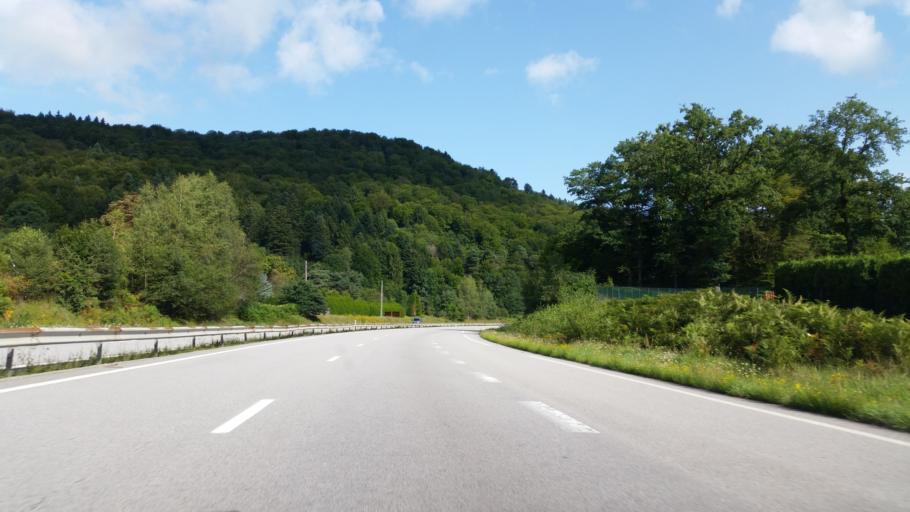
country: FR
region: Lorraine
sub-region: Departement des Vosges
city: Saint-Nabord
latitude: 48.0722
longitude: 6.5947
